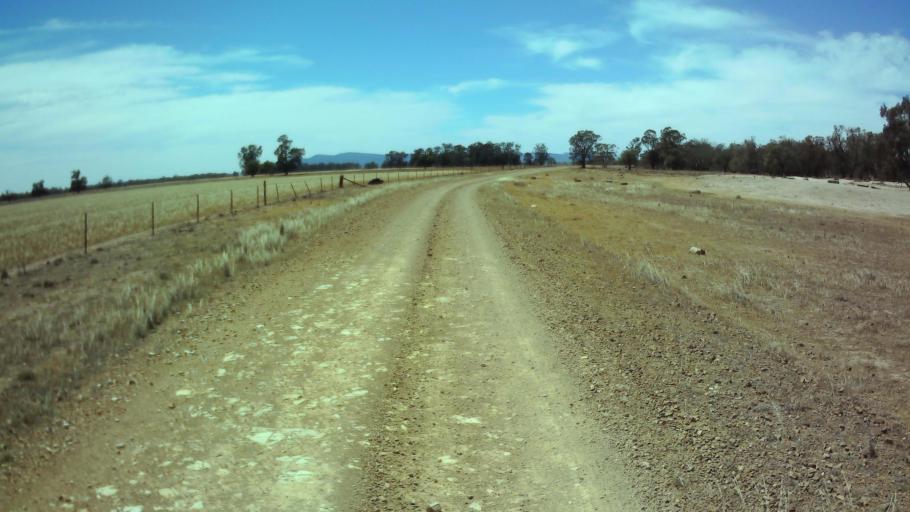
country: AU
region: New South Wales
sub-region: Weddin
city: Grenfell
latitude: -33.8604
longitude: 147.7536
